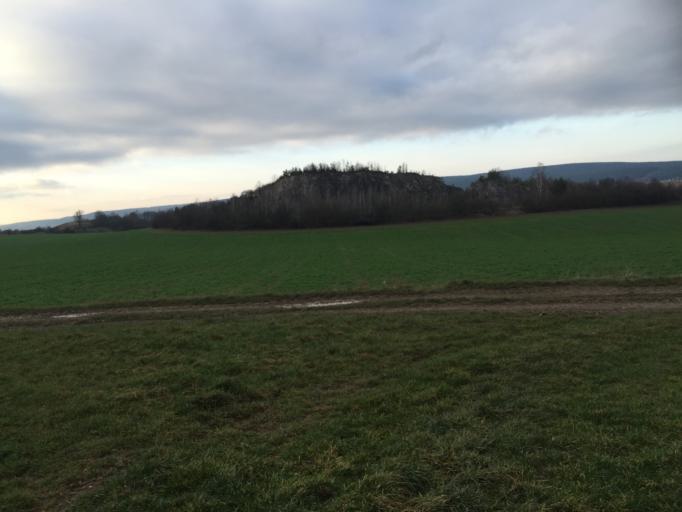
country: DE
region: Thuringia
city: Ranis
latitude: 50.6743
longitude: 11.5637
